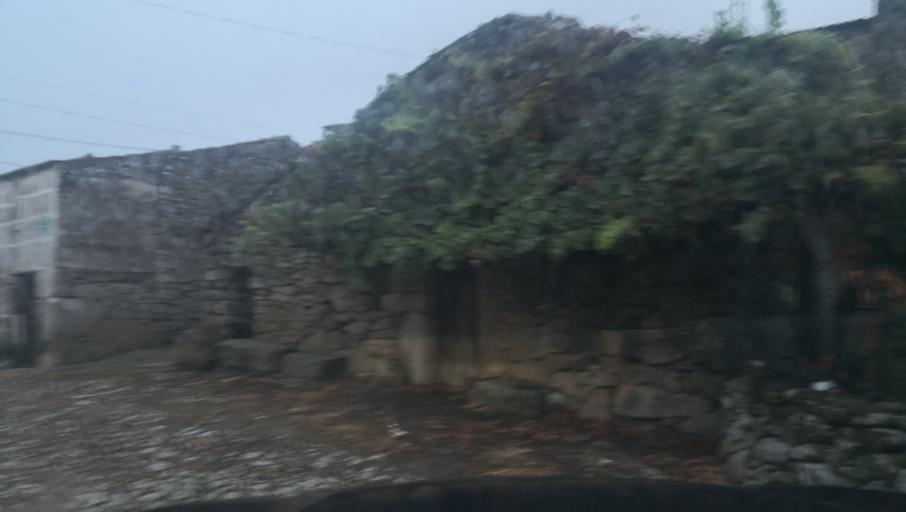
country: PT
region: Vila Real
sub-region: Sabrosa
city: Sabrosa
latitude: 41.2846
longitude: -7.5938
